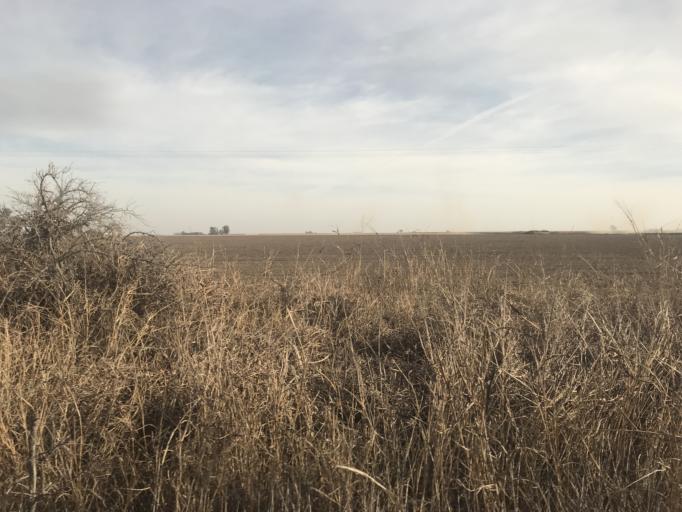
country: AR
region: Cordoba
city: Laguna Larga
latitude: -31.7485
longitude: -63.8279
